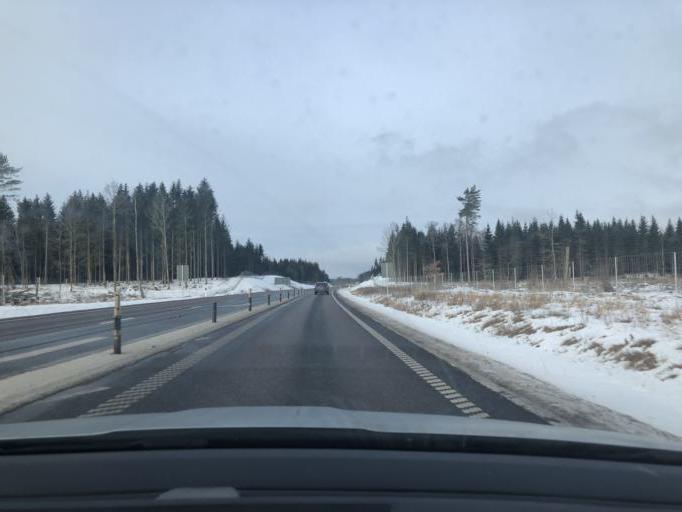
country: SE
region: OEstergoetland
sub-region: Motala Kommun
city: Borensberg
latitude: 58.5853
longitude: 15.2002
